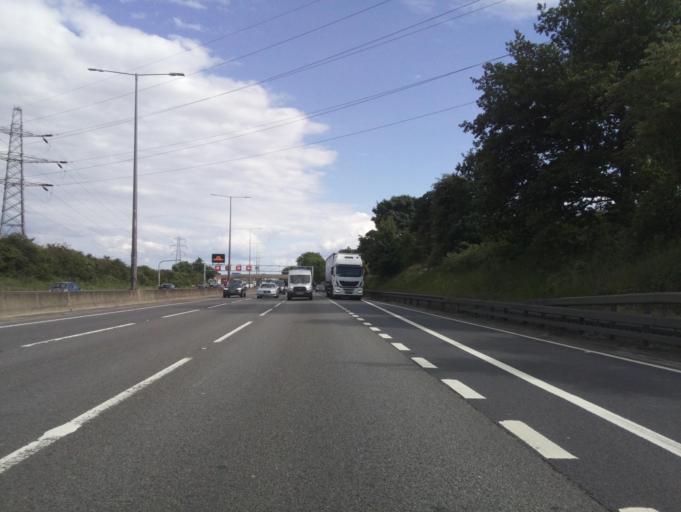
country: GB
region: England
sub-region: Central Bedfordshire
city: Caddington
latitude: 51.8633
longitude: -0.4342
